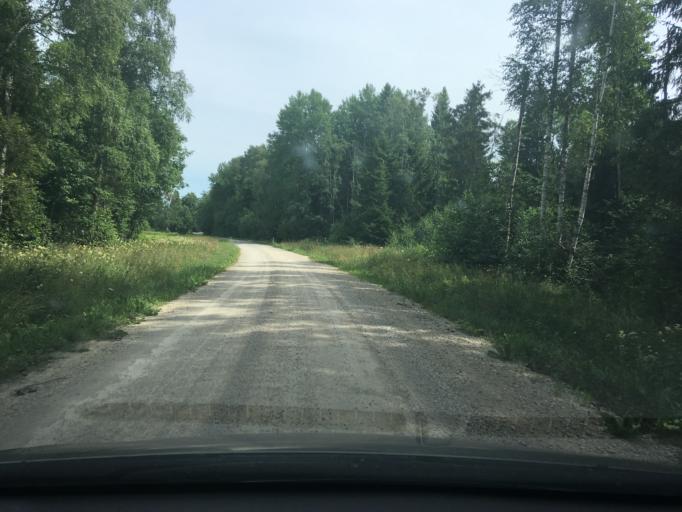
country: EE
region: Raplamaa
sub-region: Maerjamaa vald
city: Marjamaa
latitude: 58.9552
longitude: 24.5935
